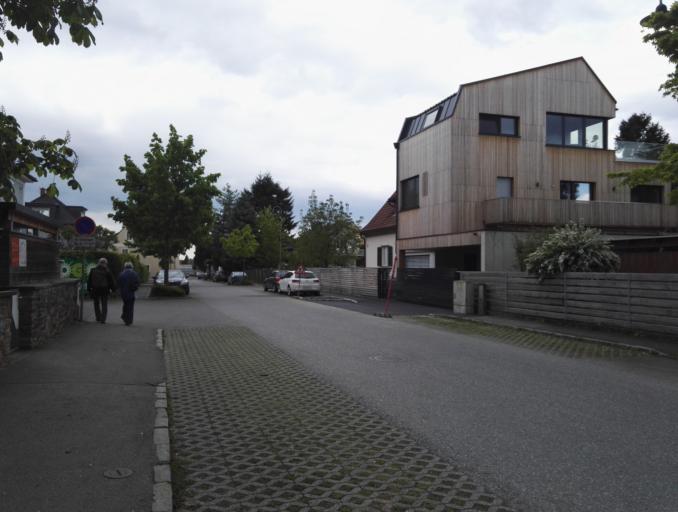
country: AT
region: Styria
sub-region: Politischer Bezirk Leibnitz
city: Leibnitz
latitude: 46.7809
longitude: 15.5438
